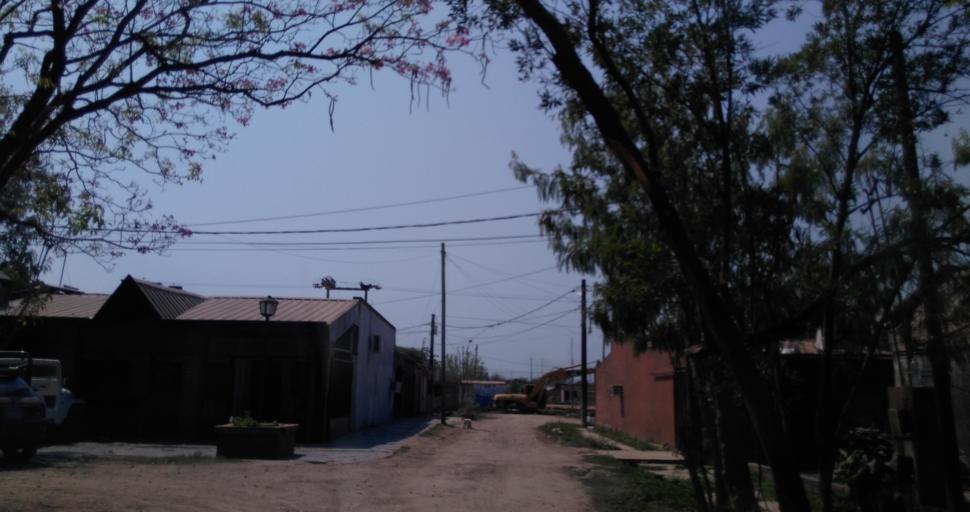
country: AR
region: Chaco
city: Fontana
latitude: -27.4238
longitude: -59.0257
